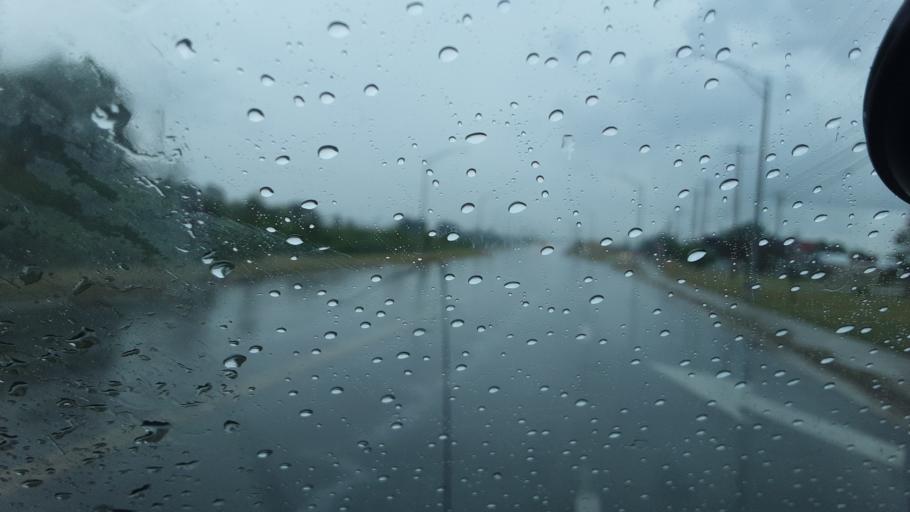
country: US
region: Ohio
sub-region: Williams County
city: Montpelier
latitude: 41.5865
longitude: -84.5892
